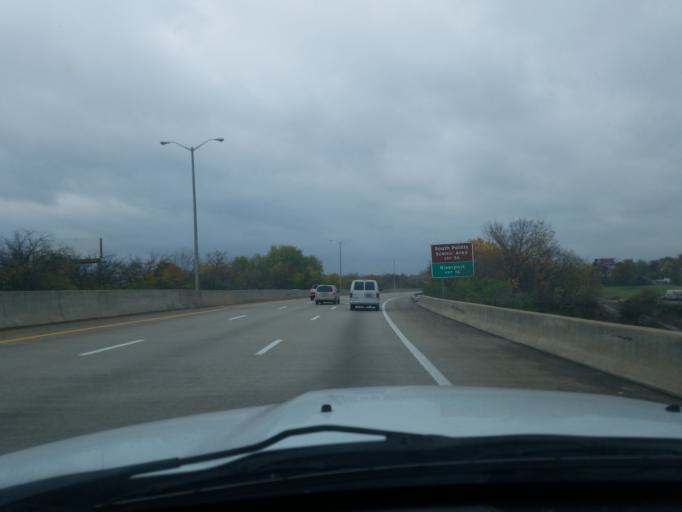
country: US
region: Kentucky
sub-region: Jefferson County
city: Shively
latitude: 38.2135
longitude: -85.8233
